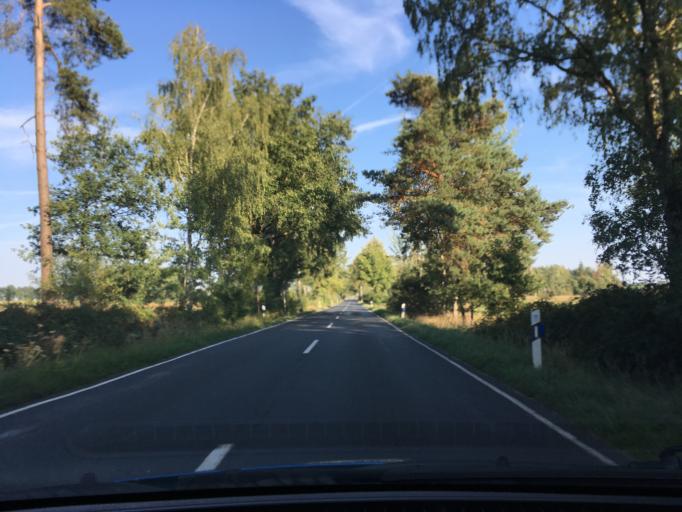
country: DE
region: Lower Saxony
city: Burgdorf
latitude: 52.4756
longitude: 9.9528
